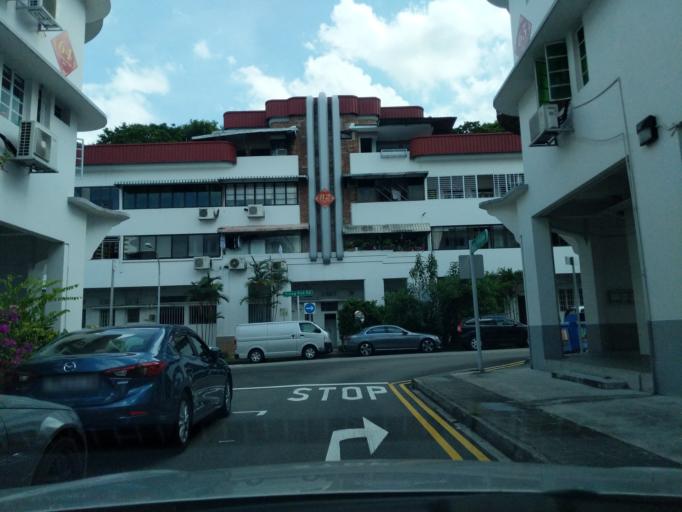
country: SG
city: Singapore
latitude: 1.2836
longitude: 103.8334
